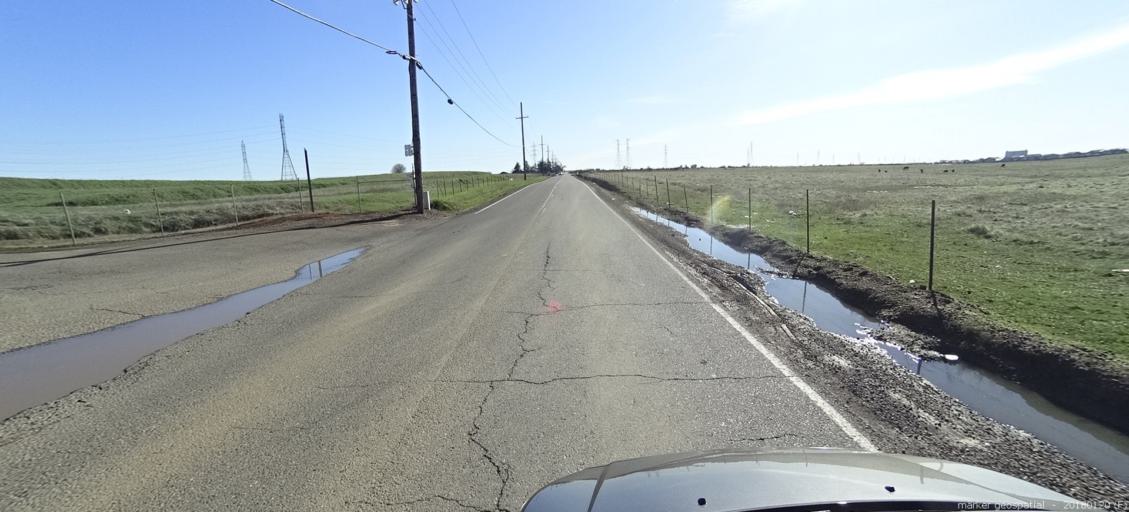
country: US
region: California
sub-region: Sacramento County
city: Gold River
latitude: 38.5794
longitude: -121.1874
